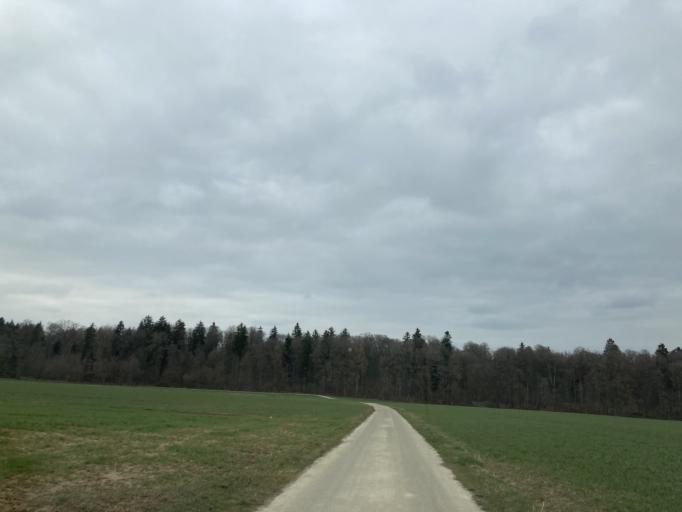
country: DE
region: Baden-Wuerttemberg
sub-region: Tuebingen Region
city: Hirrlingen
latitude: 48.4355
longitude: 8.8988
